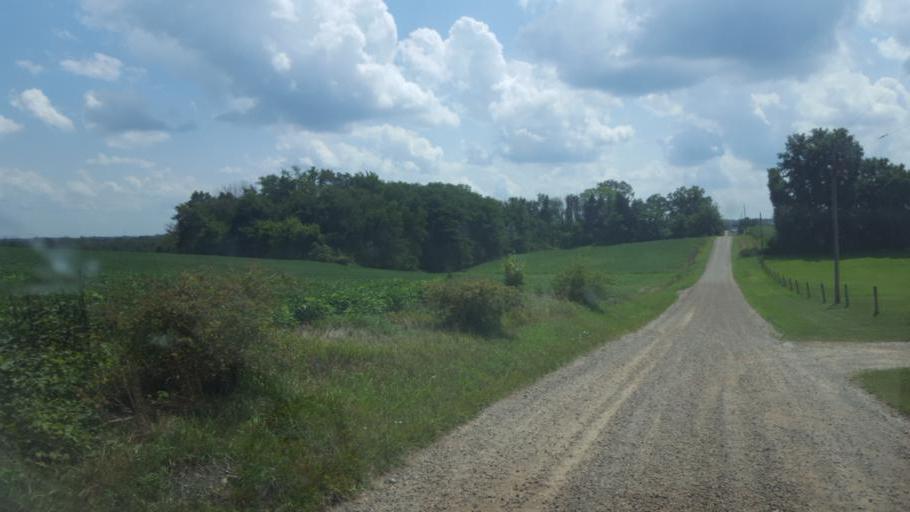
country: US
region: Ohio
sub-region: Knox County
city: Fredericktown
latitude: 40.4124
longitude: -82.5831
